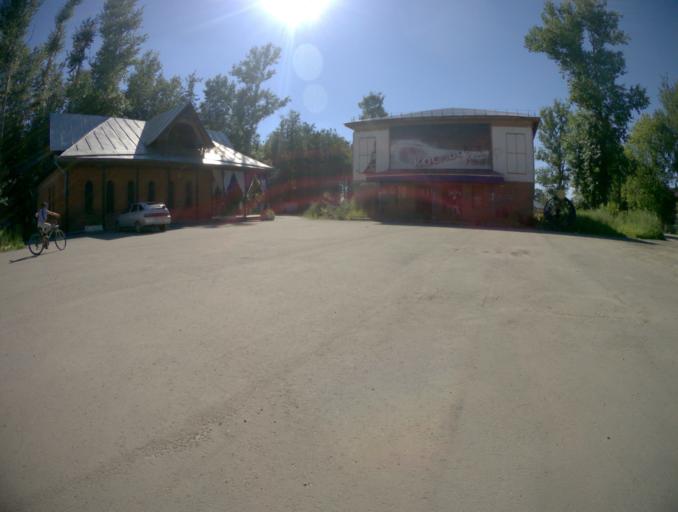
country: RU
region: Nizjnij Novgorod
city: Pavlovo
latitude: 55.9761
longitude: 43.0879
